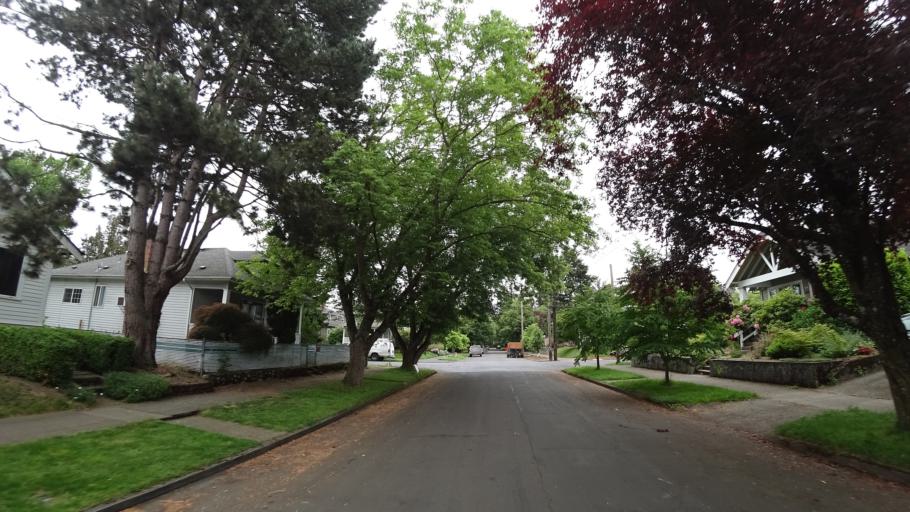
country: US
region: Oregon
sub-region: Clackamas County
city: Milwaukie
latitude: 45.4602
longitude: -122.6491
